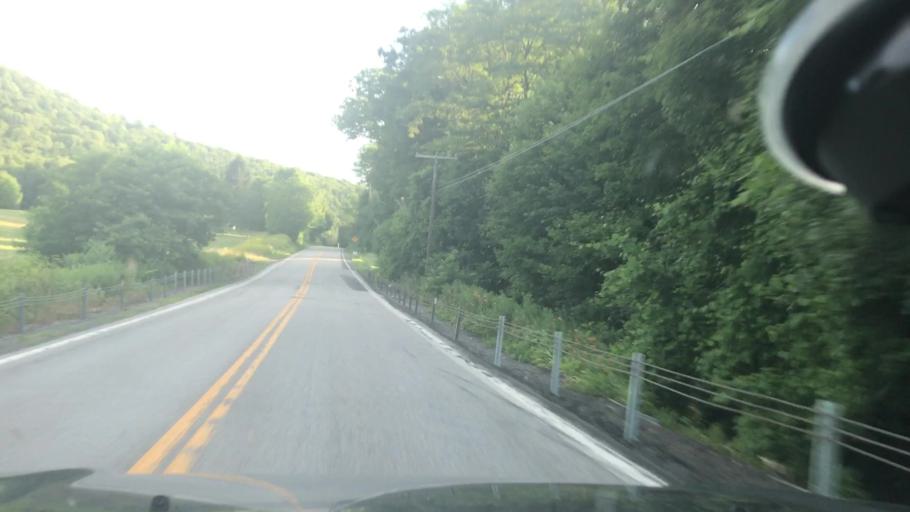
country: US
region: New York
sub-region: Otsego County
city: Unadilla
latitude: 42.3369
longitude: -75.2703
